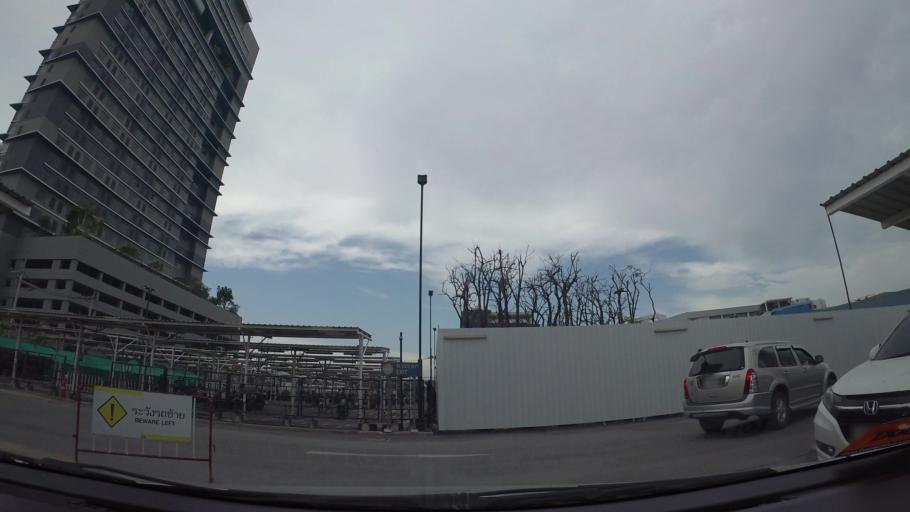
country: TH
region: Chon Buri
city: Chon Buri
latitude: 13.3357
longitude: 100.9684
